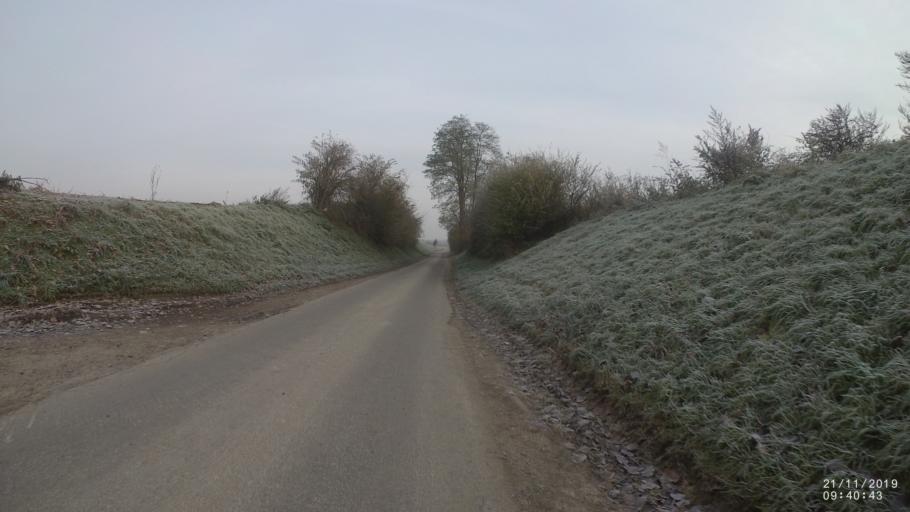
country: BE
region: Flanders
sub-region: Provincie Vlaams-Brabant
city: Tienen
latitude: 50.7764
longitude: 4.9927
